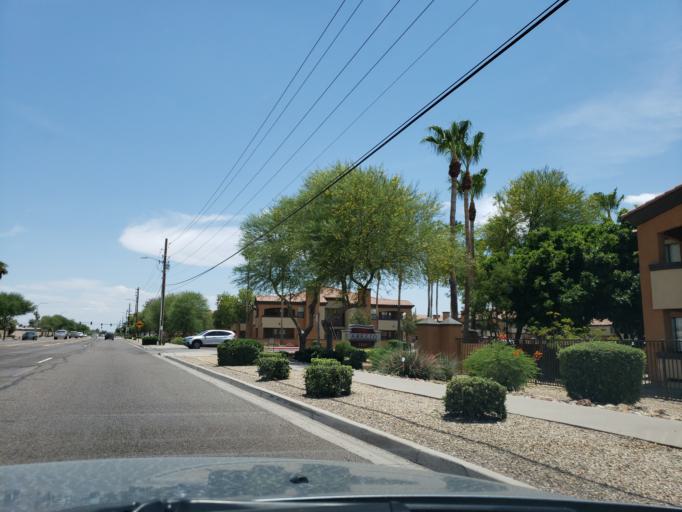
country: US
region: Arizona
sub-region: Maricopa County
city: Tolleson
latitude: 33.4656
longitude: -112.2151
